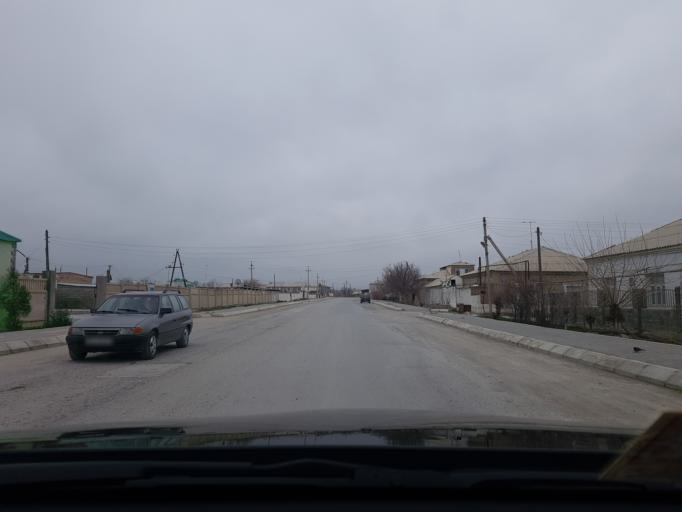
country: TM
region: Ahal
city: Abadan
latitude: 38.1476
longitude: 57.9526
